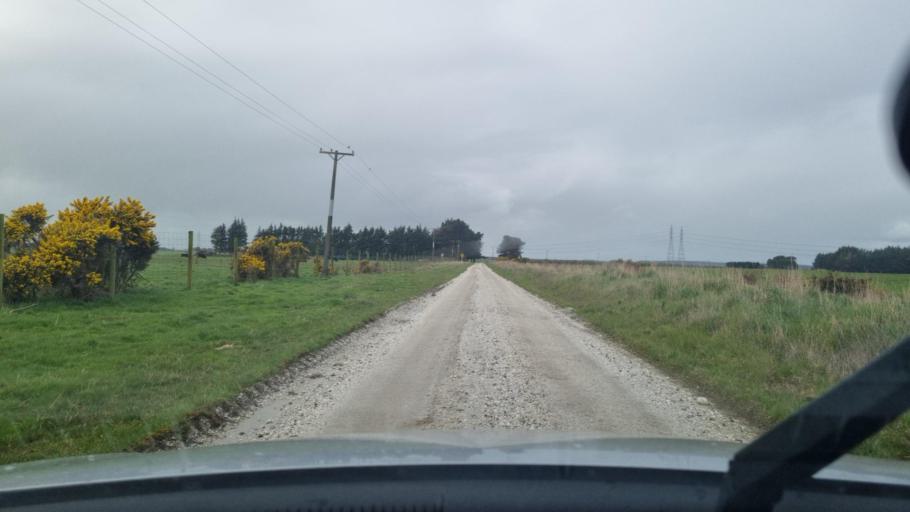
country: NZ
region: Southland
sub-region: Invercargill City
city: Invercargill
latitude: -46.4936
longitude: 168.4249
